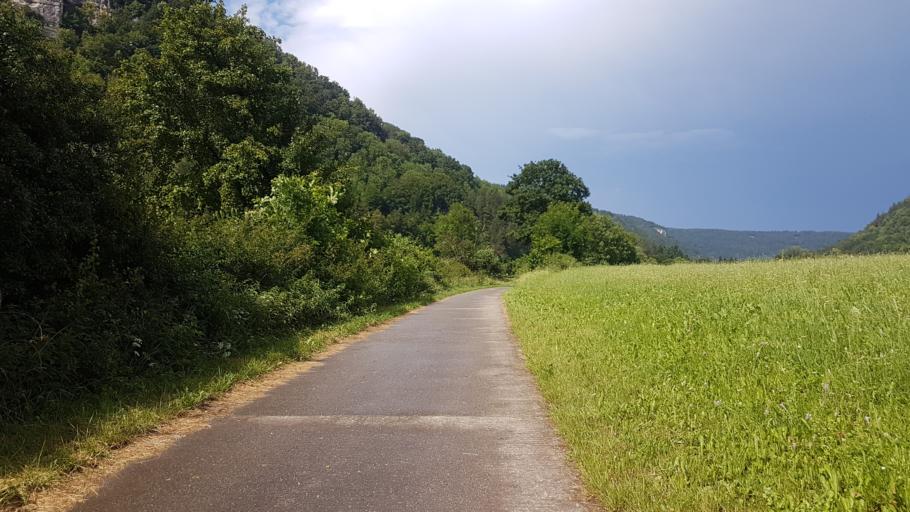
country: DE
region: Baden-Wuerttemberg
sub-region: Tuebingen Region
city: Schwenningen
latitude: 48.0787
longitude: 9.0291
